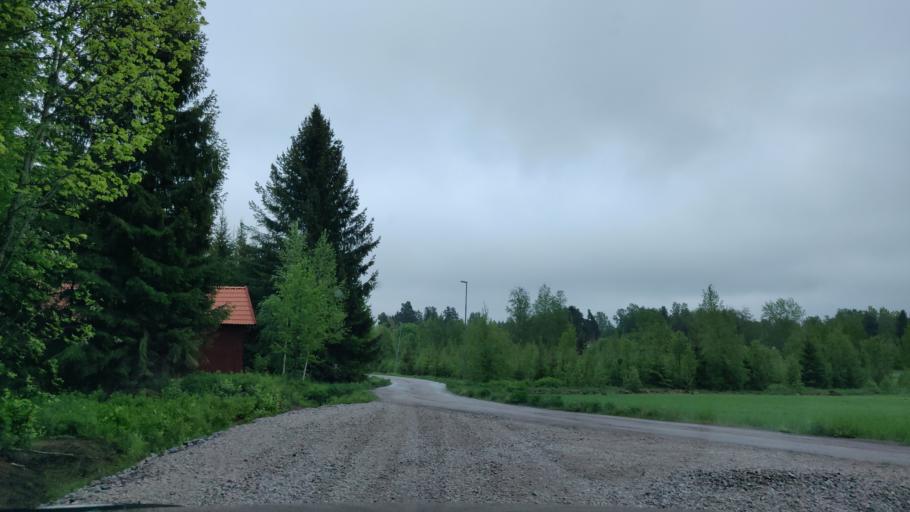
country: SE
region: Dalarna
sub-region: Avesta Kommun
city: Horndal
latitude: 60.3044
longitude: 16.4053
